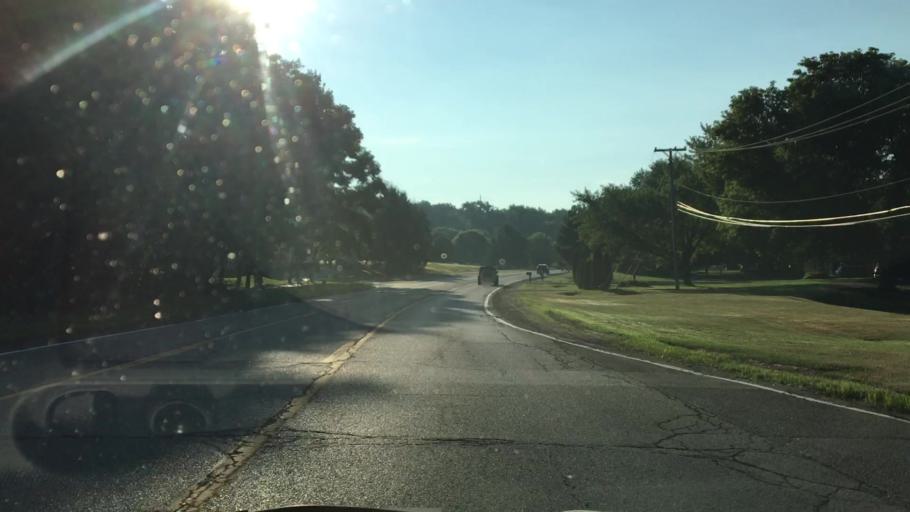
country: US
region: Michigan
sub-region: Oakland County
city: South Lyon
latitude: 42.5166
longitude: -83.6400
